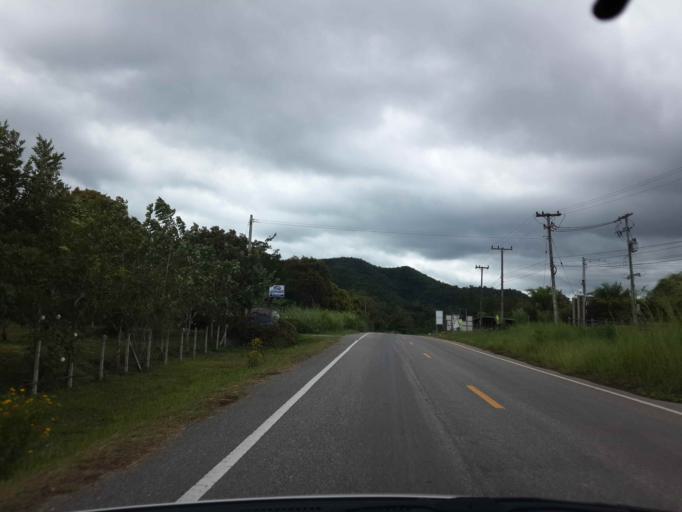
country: TH
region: Ratchaburi
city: Suan Phueng
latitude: 13.6617
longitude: 99.2094
